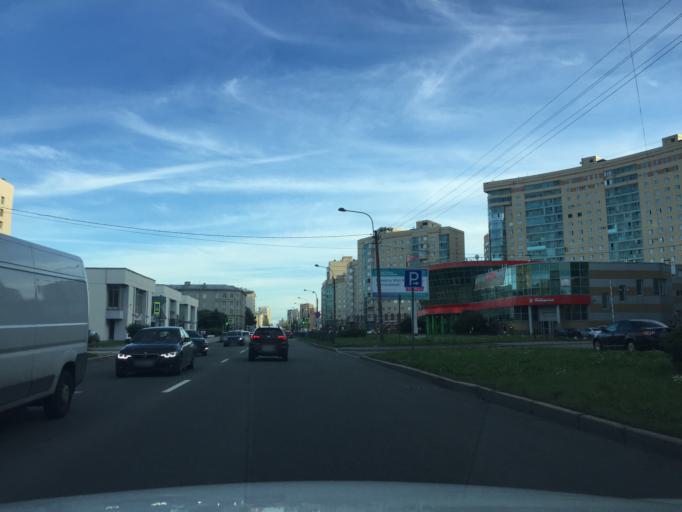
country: RU
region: St.-Petersburg
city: Kupchino
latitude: 59.8699
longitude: 30.3137
